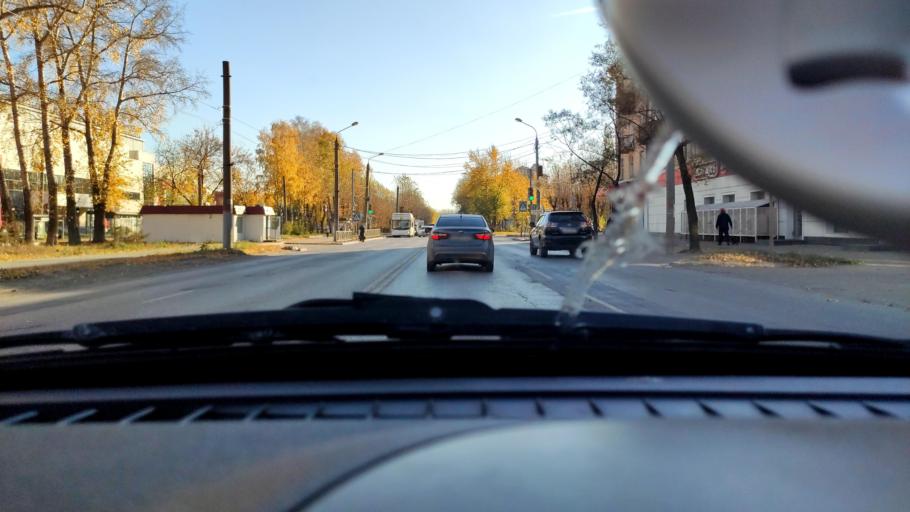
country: RU
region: Perm
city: Froly
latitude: 57.9614
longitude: 56.2436
